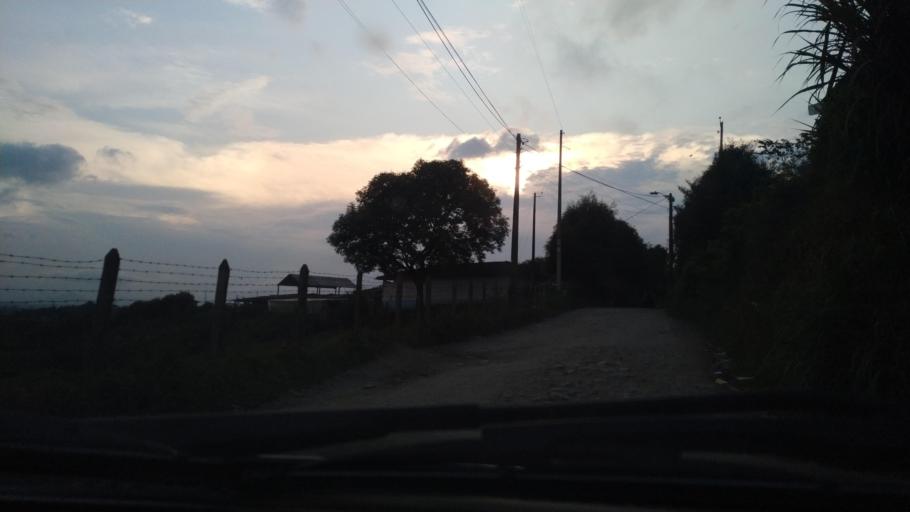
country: CO
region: Antioquia
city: Marinilla
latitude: 6.1936
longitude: -75.2851
